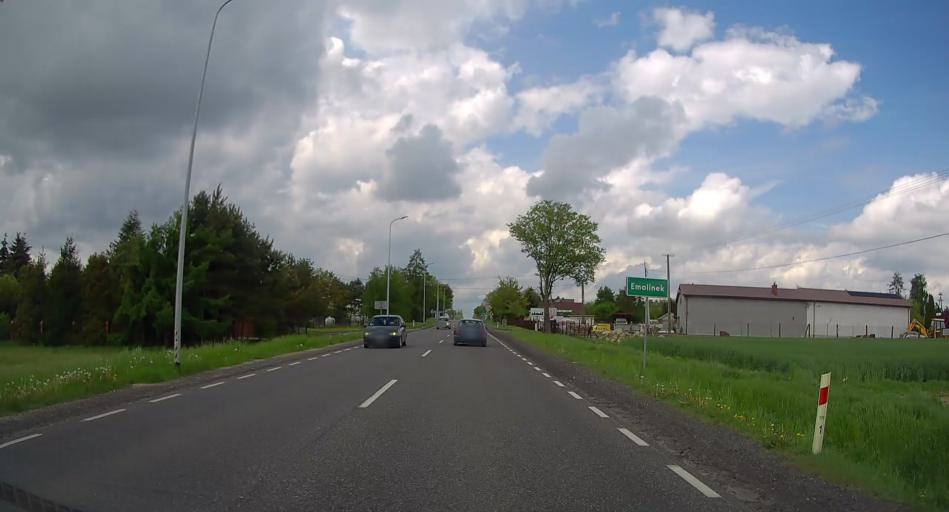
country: PL
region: Masovian Voivodeship
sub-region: Powiat plonski
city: Zaluski
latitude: 52.4439
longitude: 20.5277
